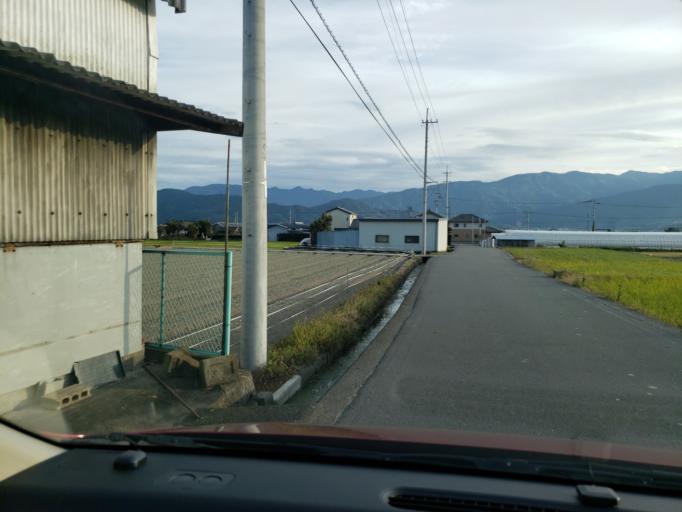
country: JP
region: Tokushima
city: Wakimachi
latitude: 34.0843
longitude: 134.2270
